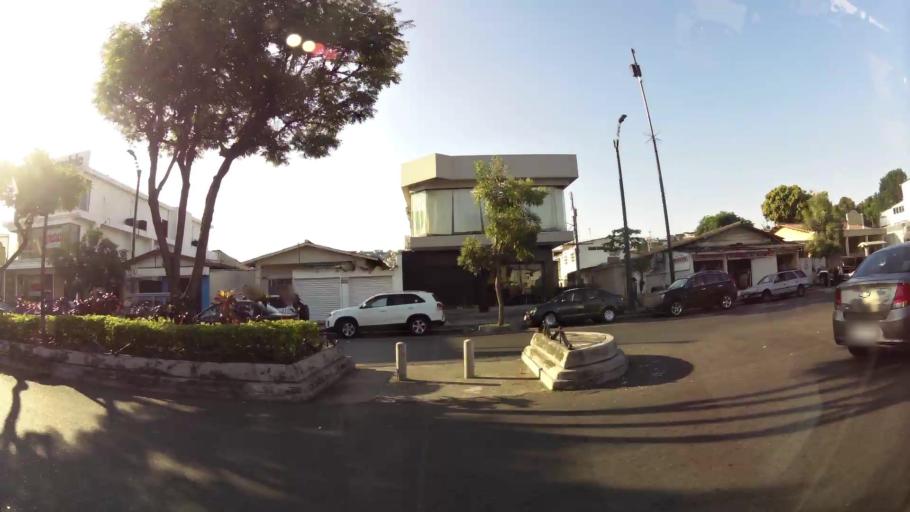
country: EC
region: Guayas
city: Guayaquil
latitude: -2.1614
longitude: -79.9168
